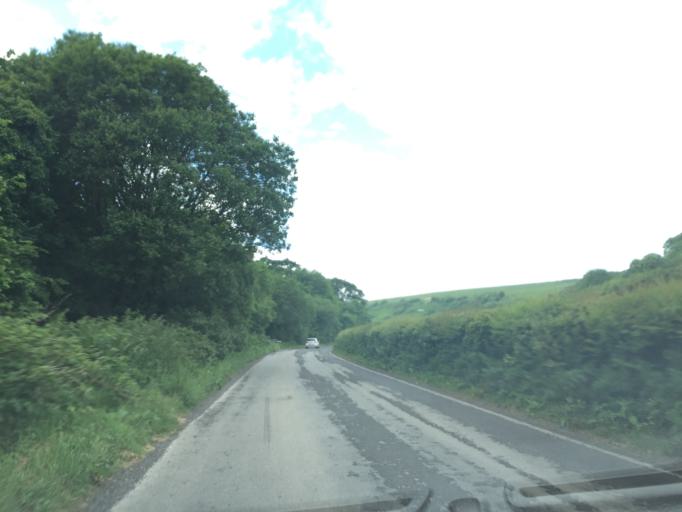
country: GB
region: England
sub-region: Dorset
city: Wool
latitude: 50.6450
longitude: -2.2668
